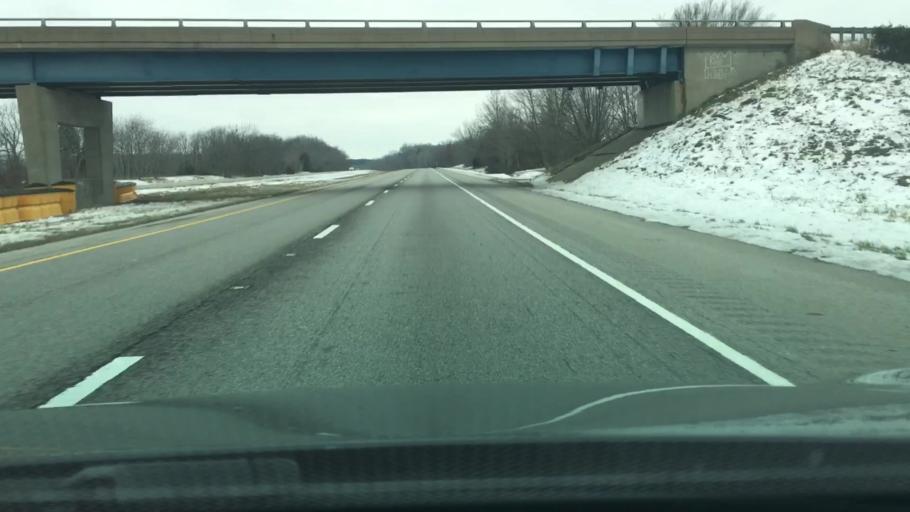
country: US
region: Illinois
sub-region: Jefferson County
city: Mount Vernon
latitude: 38.3535
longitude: -88.9919
